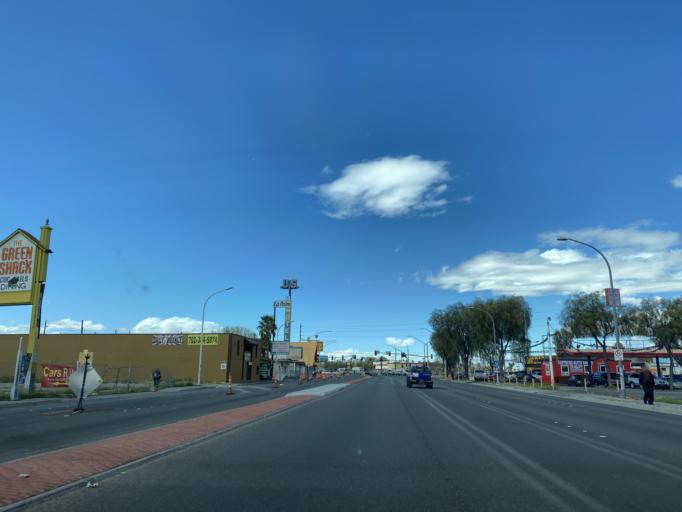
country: US
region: Nevada
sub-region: Clark County
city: Winchester
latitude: 36.1575
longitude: -115.1150
